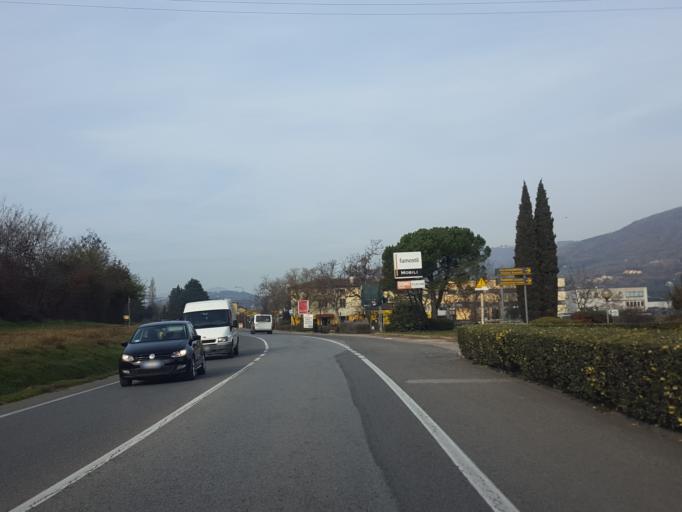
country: IT
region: Veneto
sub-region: Provincia di Verona
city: Costermano
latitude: 45.5837
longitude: 10.7516
